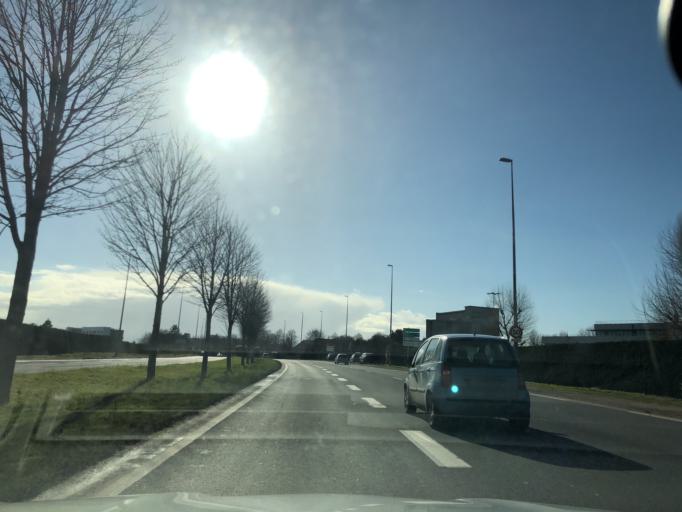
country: FR
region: Lower Normandy
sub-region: Departement du Calvados
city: Caen
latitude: 49.2042
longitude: -0.3519
